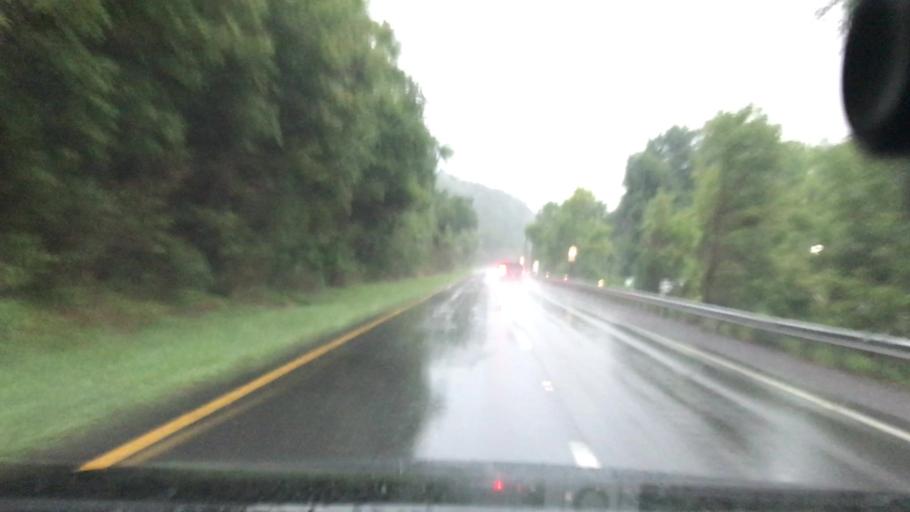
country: US
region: Virginia
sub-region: Giles County
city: Narrows
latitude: 37.3767
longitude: -80.8217
